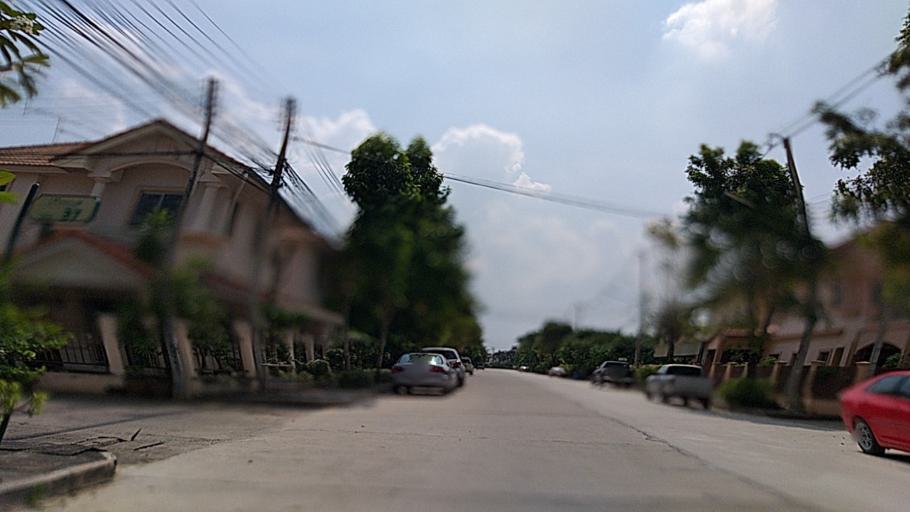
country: TH
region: Pathum Thani
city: Ban Rangsit
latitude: 14.0404
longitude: 100.7653
